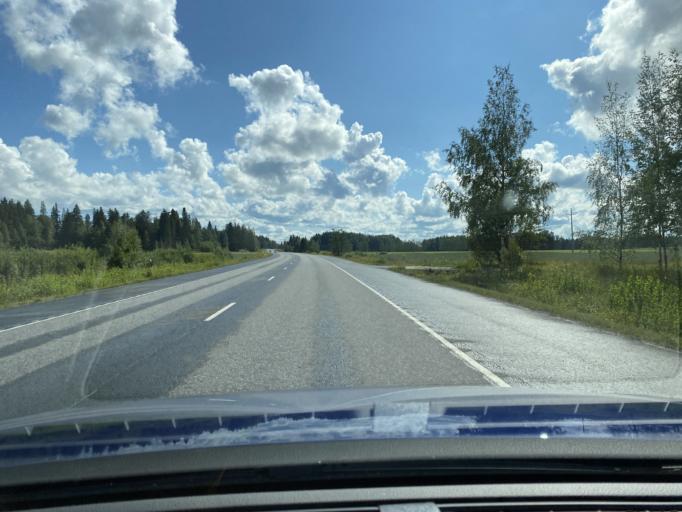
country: FI
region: Pirkanmaa
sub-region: Tampere
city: Lempaeaelae
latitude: 61.3328
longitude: 23.7782
